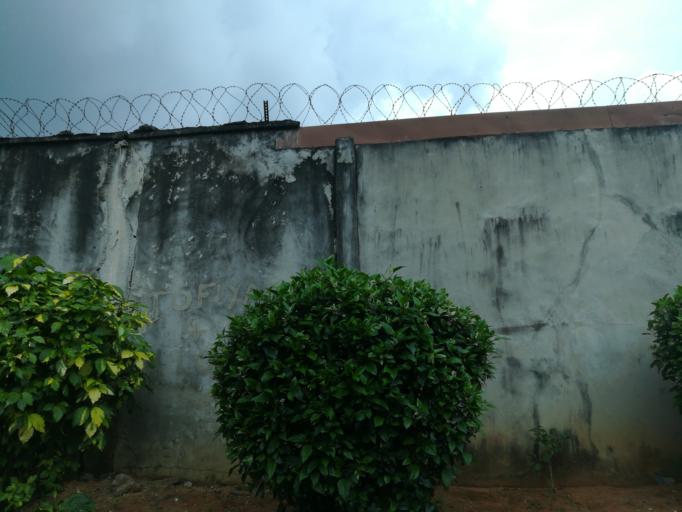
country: NG
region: Rivers
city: Port Harcourt
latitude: 4.8185
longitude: 7.0695
